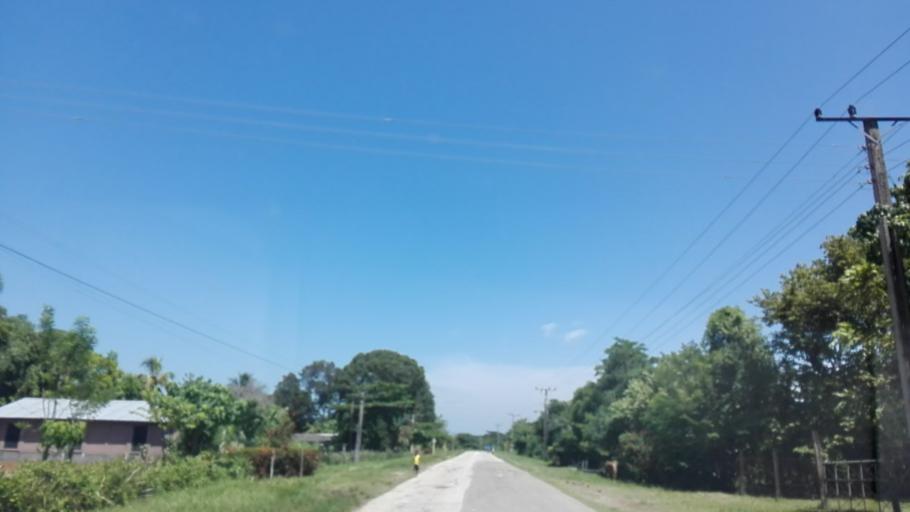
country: CU
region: Granma
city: Bartolome Maso
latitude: 20.1414
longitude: -76.9465
